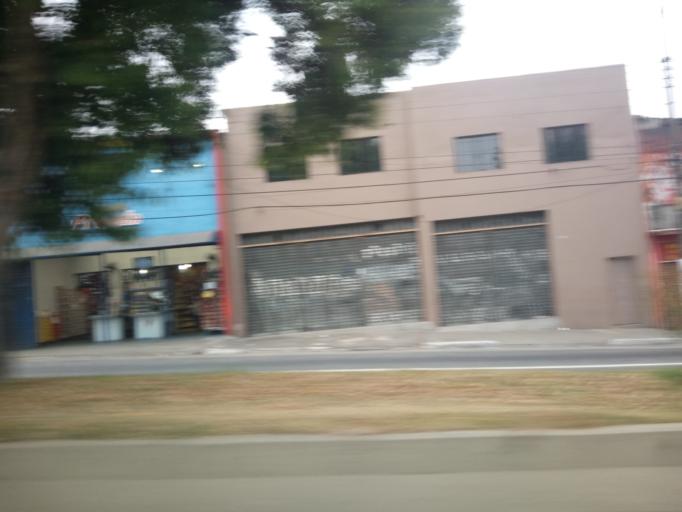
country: BR
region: Sao Paulo
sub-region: Diadema
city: Diadema
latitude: -23.6652
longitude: -46.6380
